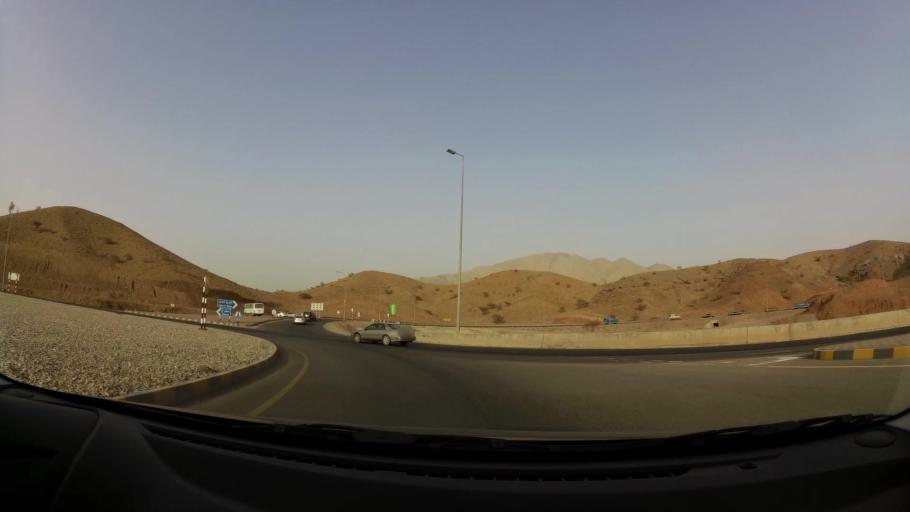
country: OM
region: Muhafazat Masqat
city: Bawshar
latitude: 23.5199
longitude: 58.3471
